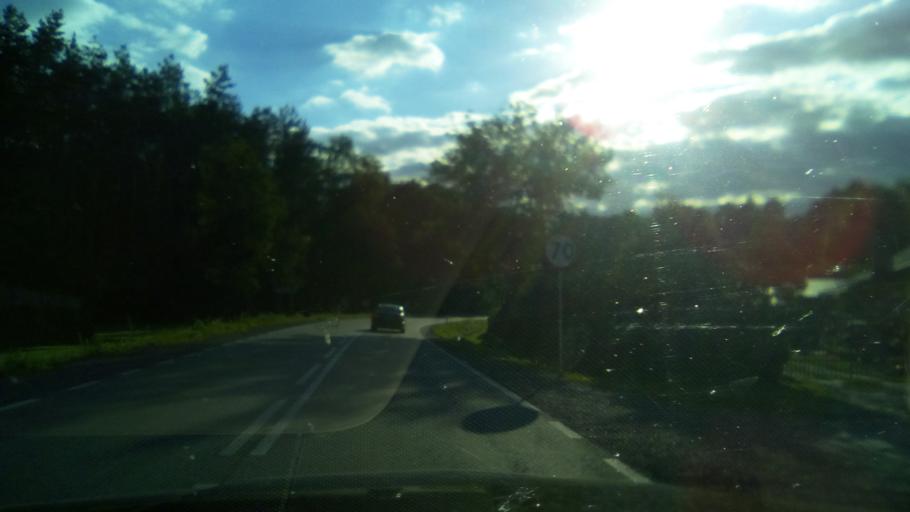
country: PL
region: Masovian Voivodeship
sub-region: Powiat bialobrzeski
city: Stromiec
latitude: 51.6474
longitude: 21.0422
